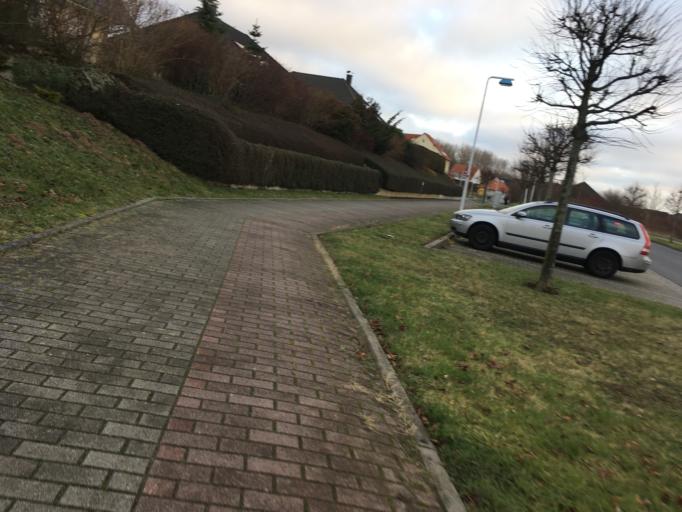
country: DE
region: Mecklenburg-Vorpommern
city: Sassnitz
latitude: 54.5121
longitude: 13.6054
